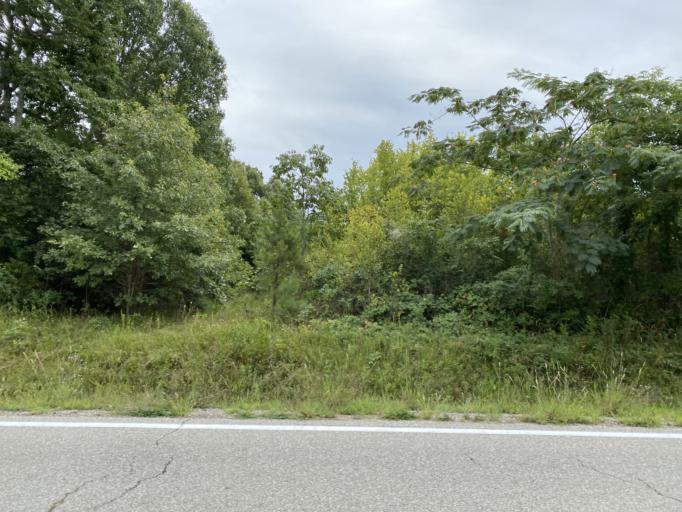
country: US
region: Arkansas
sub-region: Fulton County
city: Salem
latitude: 36.4286
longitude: -91.7027
